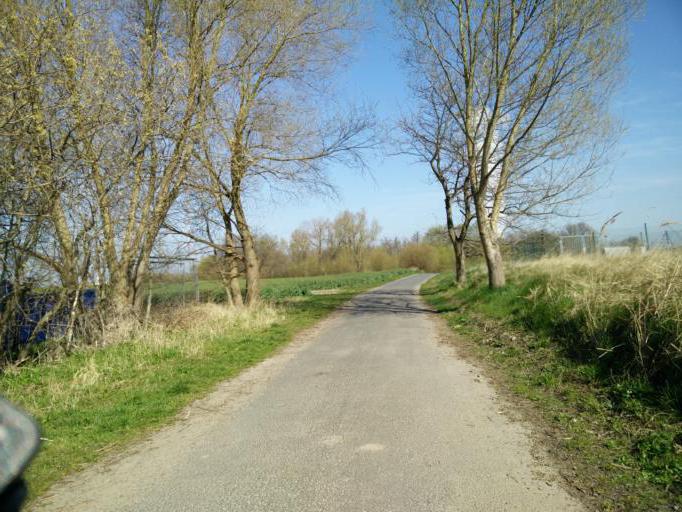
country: DE
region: Mecklenburg-Vorpommern
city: Dierkow-West
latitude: 54.1221
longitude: 12.1353
